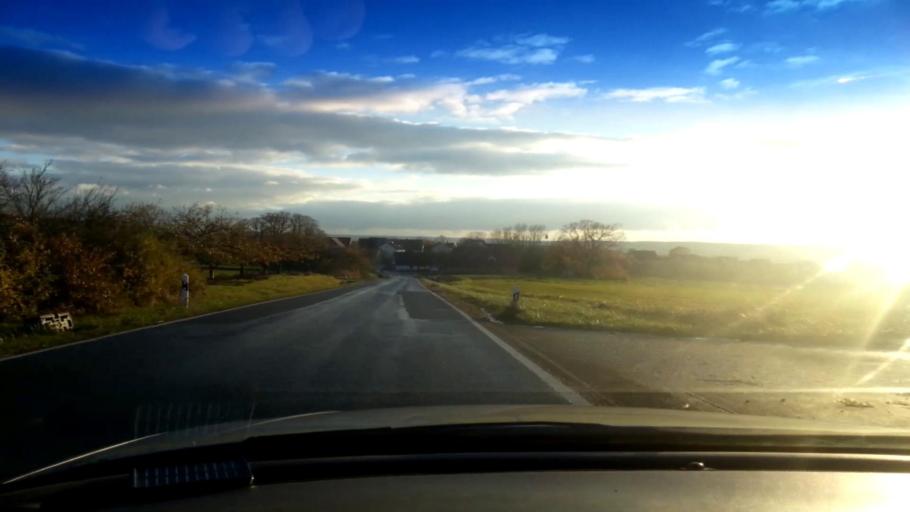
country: DE
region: Bavaria
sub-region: Upper Franconia
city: Buttenheim
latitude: 49.8306
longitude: 11.0292
